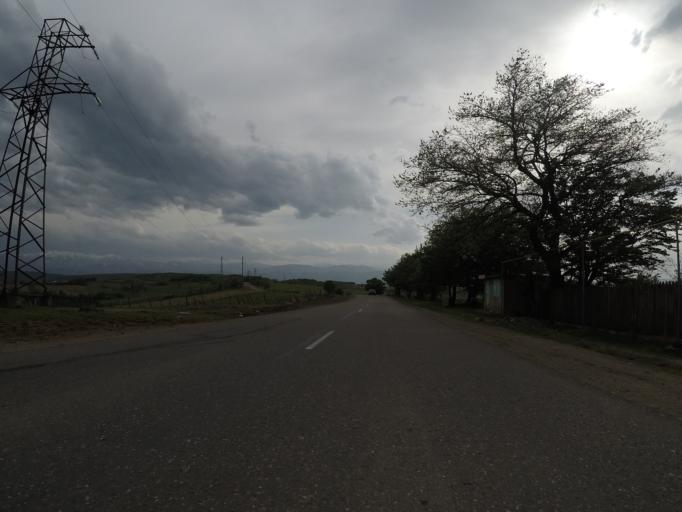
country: GE
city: Shorapani
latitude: 42.1851
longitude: 43.1388
